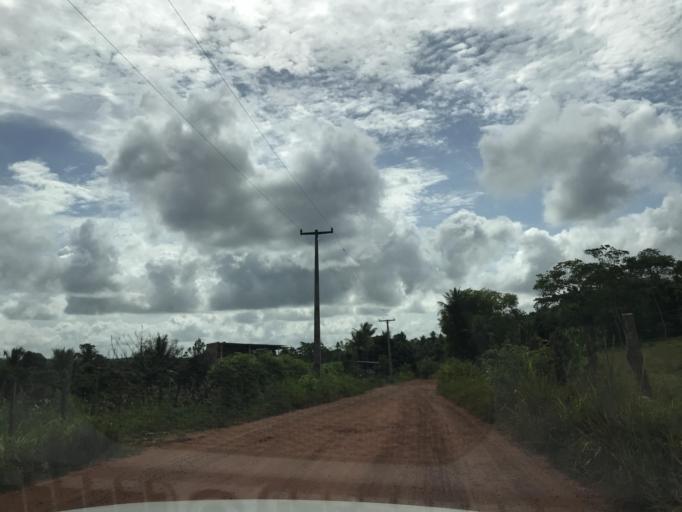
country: BR
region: Bahia
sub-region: Entre Rios
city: Entre Rios
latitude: -12.1671
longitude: -38.1555
